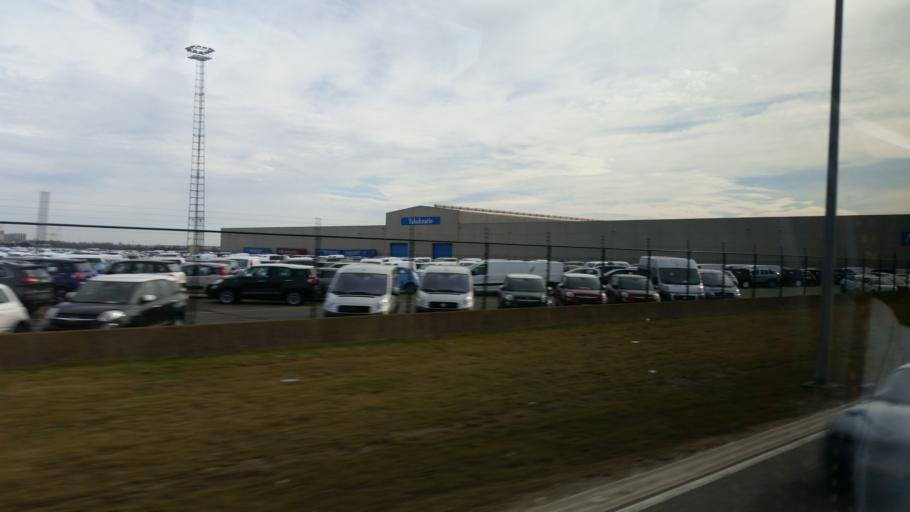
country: BE
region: Flanders
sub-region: Provincie Oost-Vlaanderen
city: Beveren
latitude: 51.2702
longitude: 4.2011
